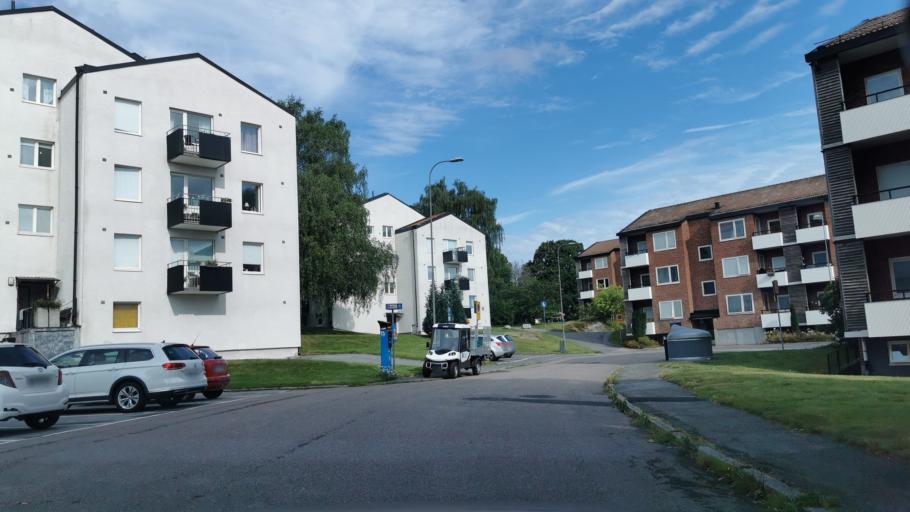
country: SE
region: Vaestra Goetaland
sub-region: Goteborg
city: Majorna
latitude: 57.6582
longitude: 11.9297
